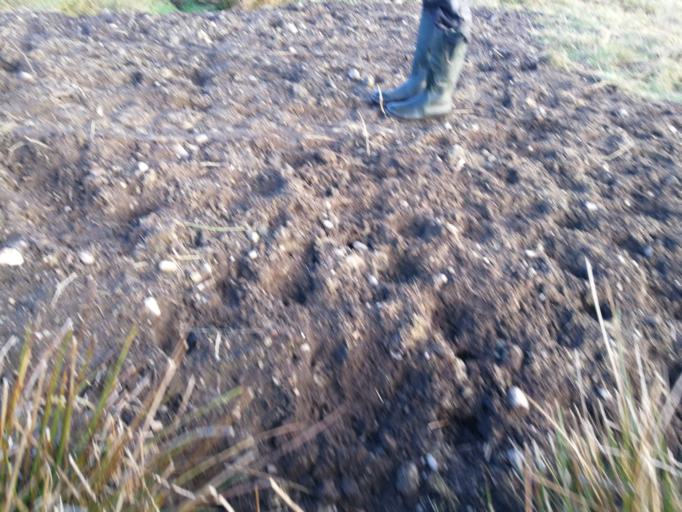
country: PL
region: Warmian-Masurian Voivodeship
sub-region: Powiat dzialdowski
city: Rybno
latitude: 53.4119
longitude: 19.9099
